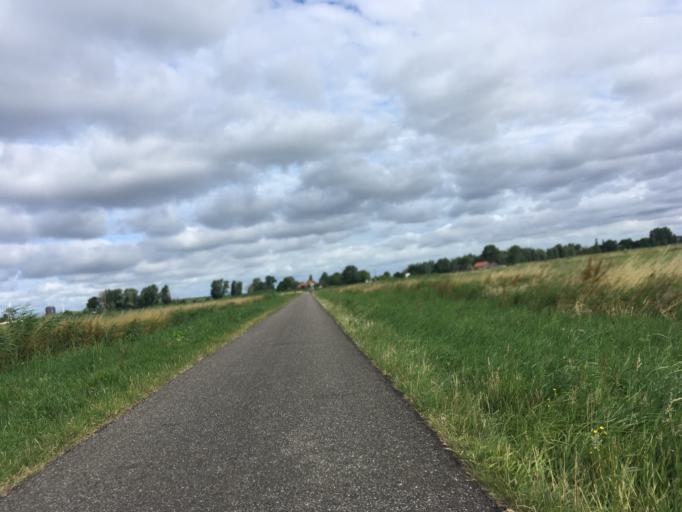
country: NL
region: North Holland
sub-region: Gemeente Haarlem
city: Haarlem
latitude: 52.3985
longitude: 4.6855
